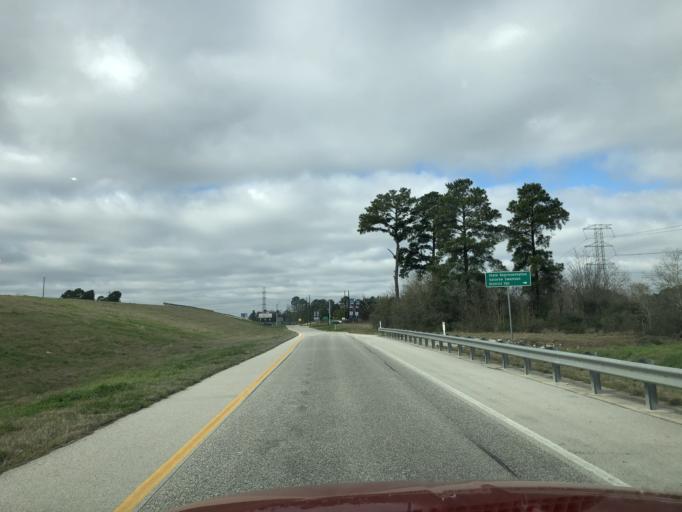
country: US
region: Texas
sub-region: Montgomery County
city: The Woodlands
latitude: 30.0949
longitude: -95.5043
